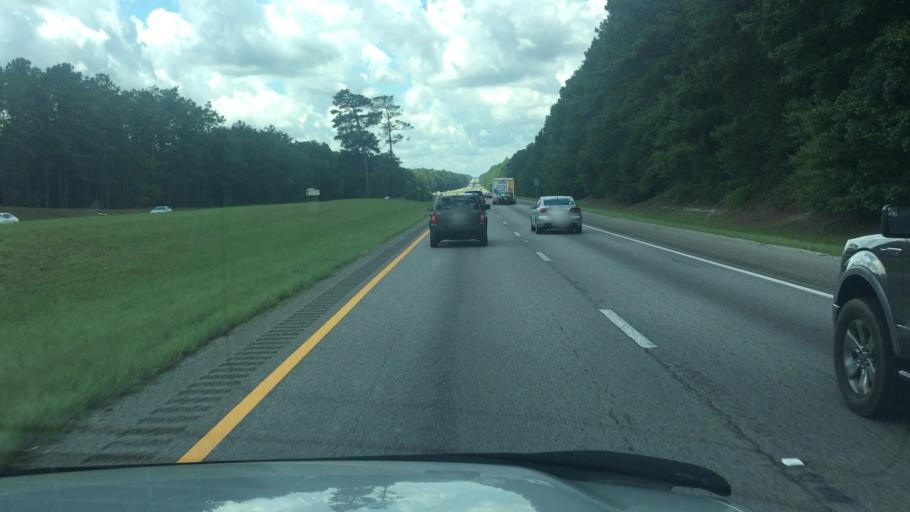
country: US
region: South Carolina
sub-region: Kershaw County
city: Elgin
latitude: 34.1382
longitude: -80.7576
